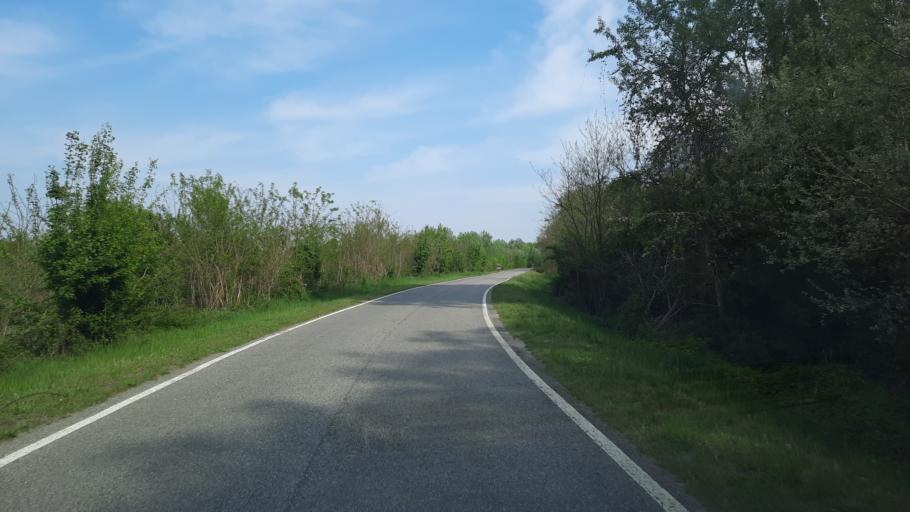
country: IT
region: Piedmont
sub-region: Provincia di Alessandria
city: Camino
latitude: 45.1747
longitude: 8.2804
